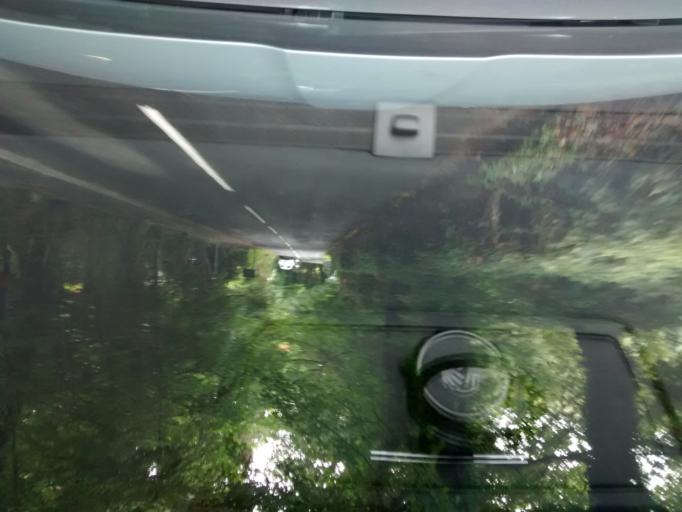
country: GB
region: Scotland
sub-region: North Ayrshire
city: Isle of Arran
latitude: 55.5855
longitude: -5.1630
